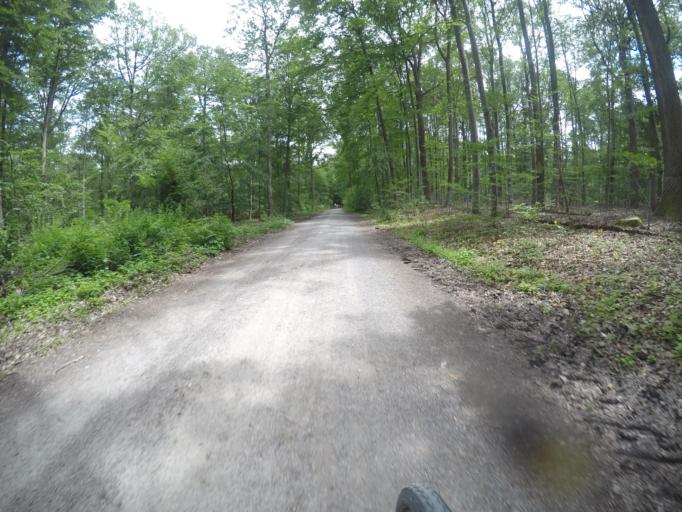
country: DE
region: Baden-Wuerttemberg
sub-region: Regierungsbezirk Stuttgart
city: Nufringen
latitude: 48.6007
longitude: 8.9066
